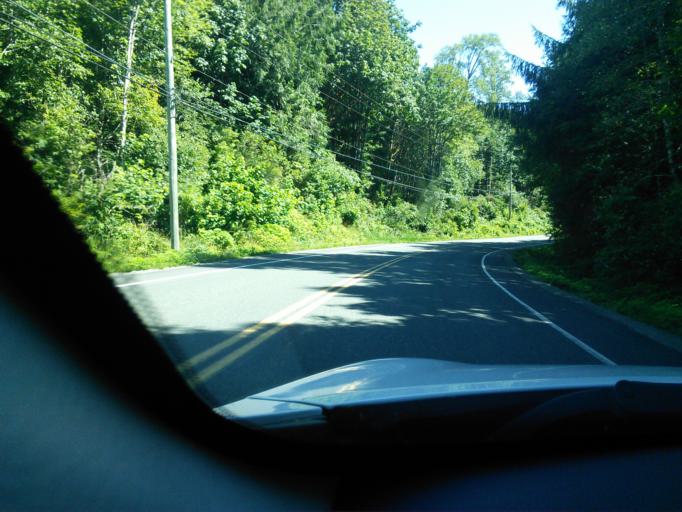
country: CA
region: British Columbia
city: Campbell River
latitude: 50.3509
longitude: -125.9060
